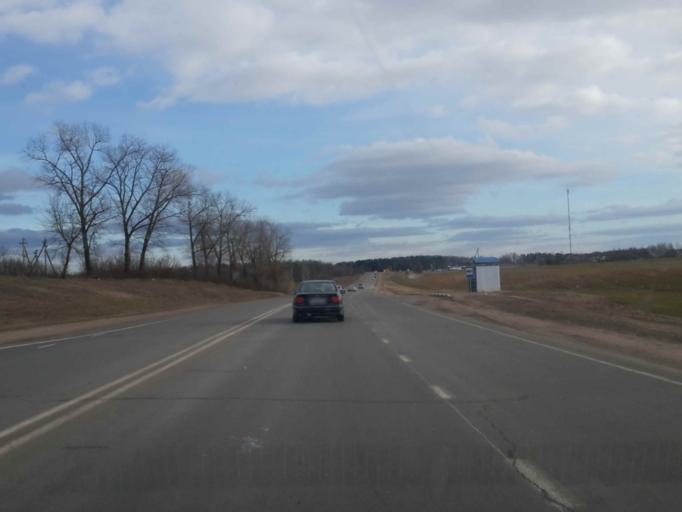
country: BY
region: Minsk
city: Bal'shavik
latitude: 54.0770
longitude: 27.5641
